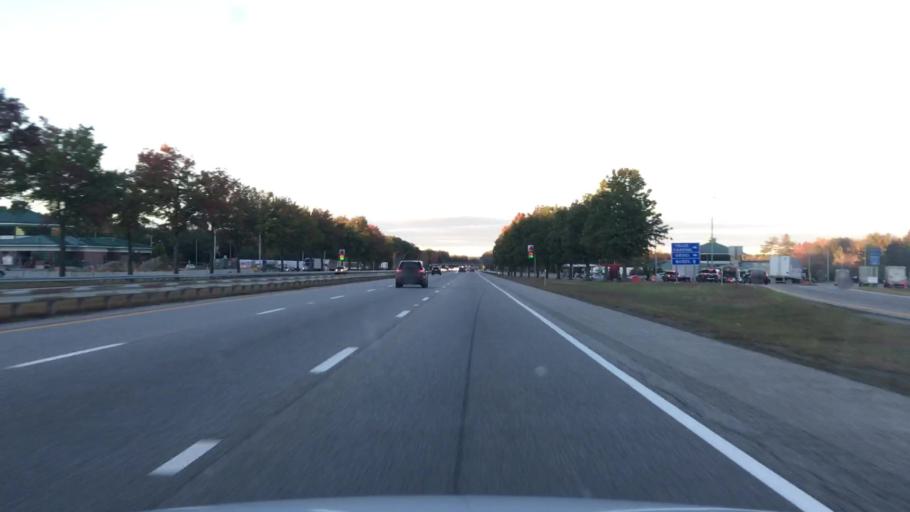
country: US
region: Maine
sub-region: York County
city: West Kennebunk
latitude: 43.4081
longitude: -70.5607
